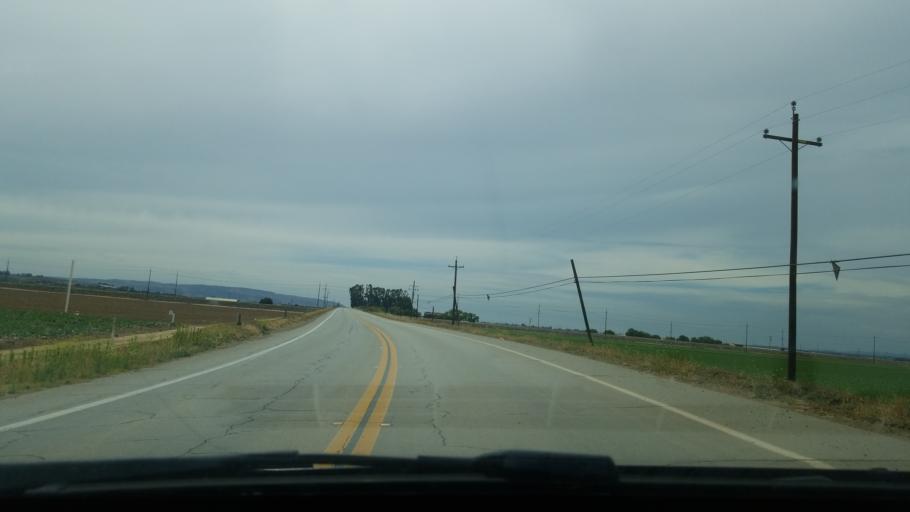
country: US
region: California
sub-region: Santa Barbara County
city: Santa Maria
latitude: 34.9232
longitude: -120.3511
